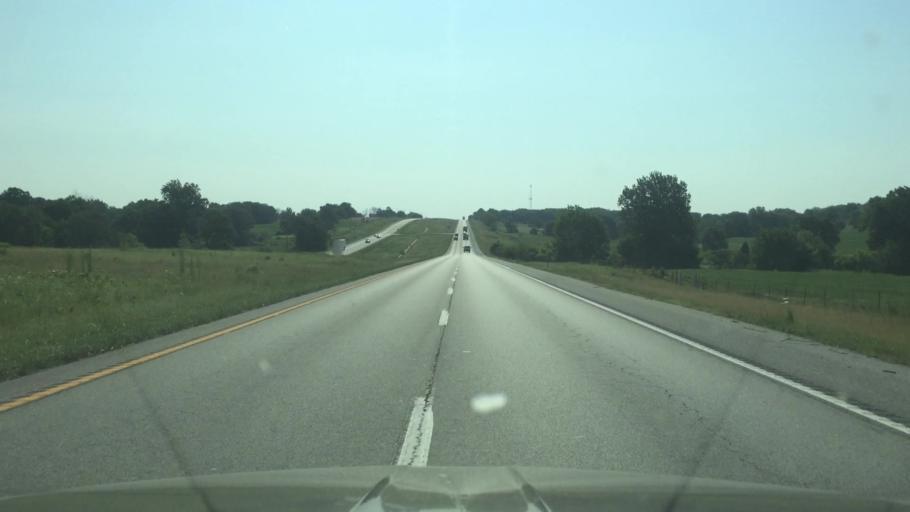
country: US
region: Missouri
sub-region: Jackson County
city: Lone Jack
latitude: 38.8692
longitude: -94.1054
